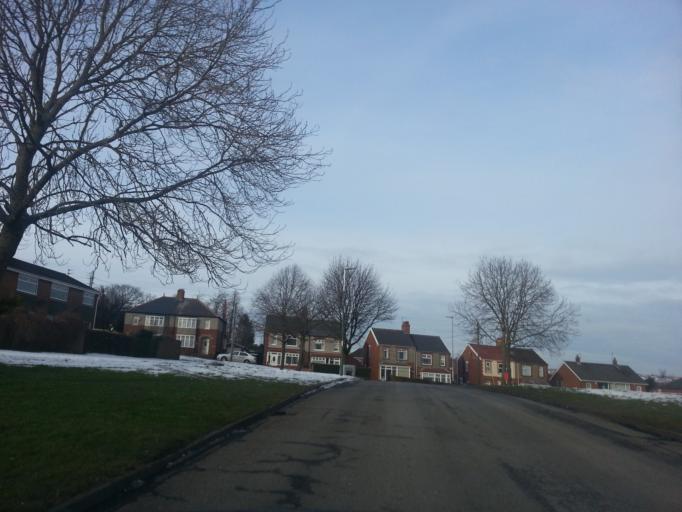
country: GB
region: England
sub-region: County Durham
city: Crook
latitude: 54.7115
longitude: -1.7569
